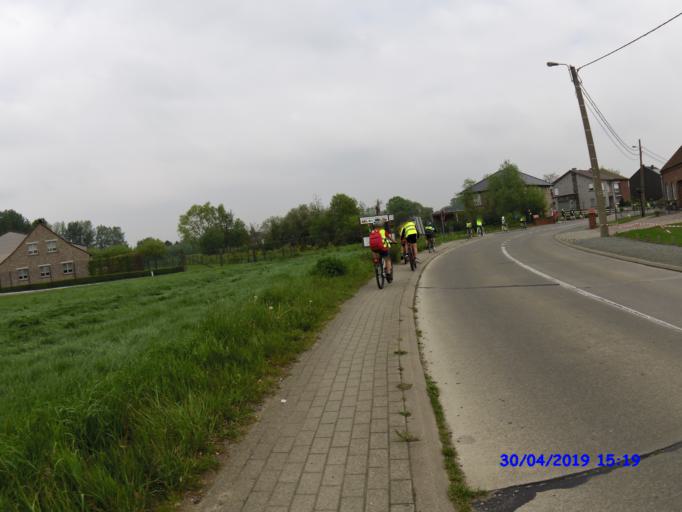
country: BE
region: Flanders
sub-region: Provincie Vlaams-Brabant
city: Opwijk
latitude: 50.9852
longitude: 4.1642
